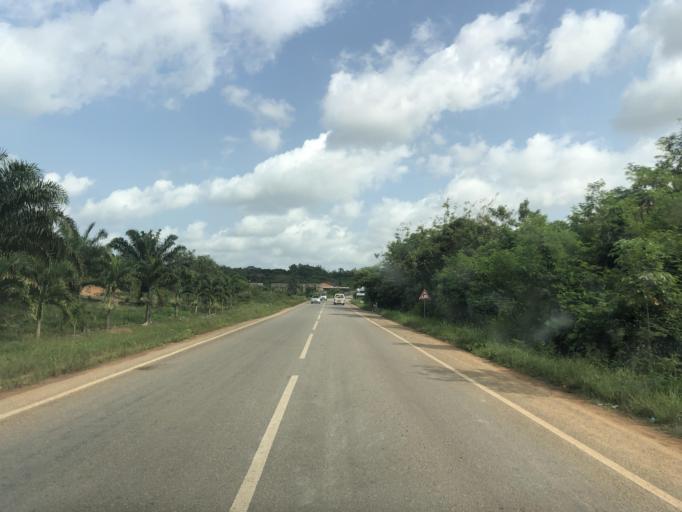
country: GH
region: Central
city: Cape Coast
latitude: 5.1918
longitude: -1.3160
